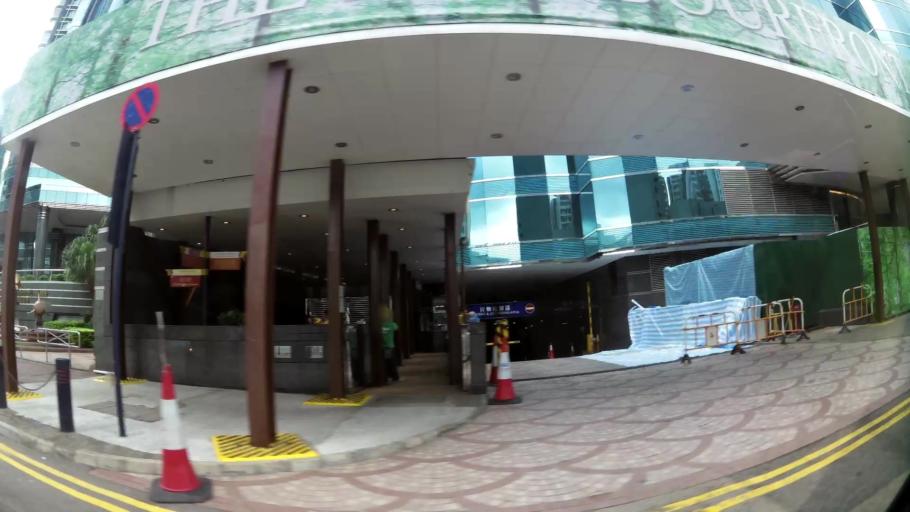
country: HK
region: Kowloon City
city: Kowloon
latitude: 22.3033
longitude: 114.1919
